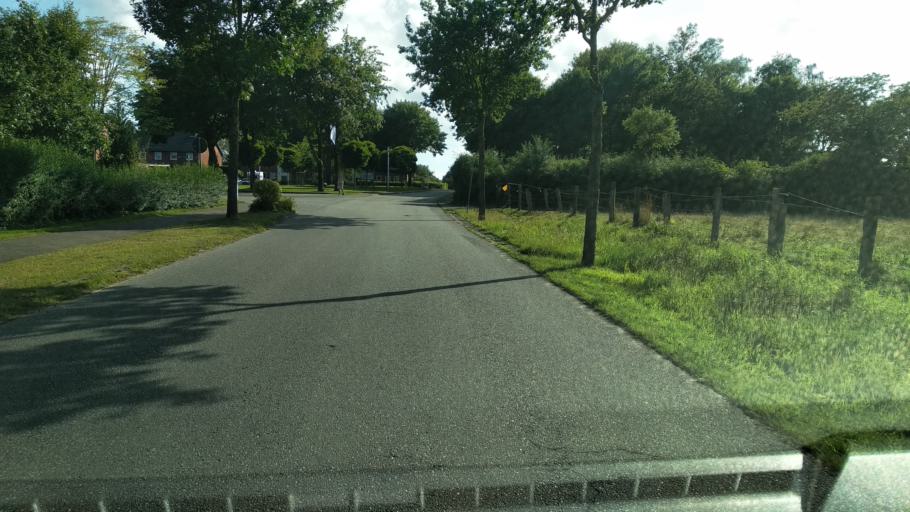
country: DE
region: Schleswig-Holstein
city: Busdorf
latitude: 54.4888
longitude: 9.5473
